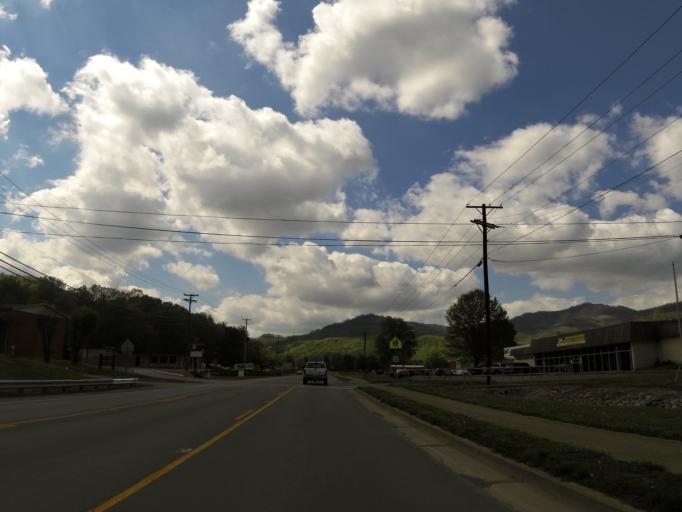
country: US
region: Kentucky
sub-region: Bell County
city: Middlesboro
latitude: 36.6069
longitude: -83.7469
